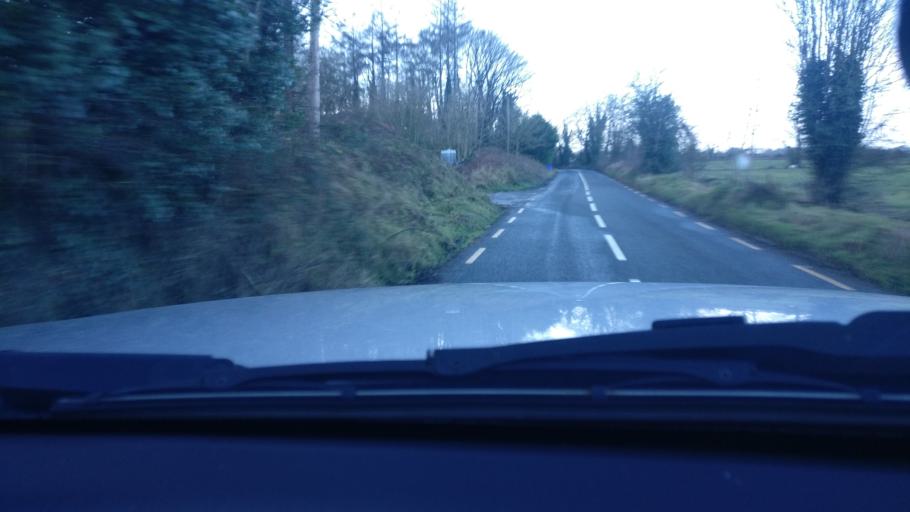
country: IE
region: Connaught
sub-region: County Galway
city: Loughrea
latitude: 53.2238
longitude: -8.3887
